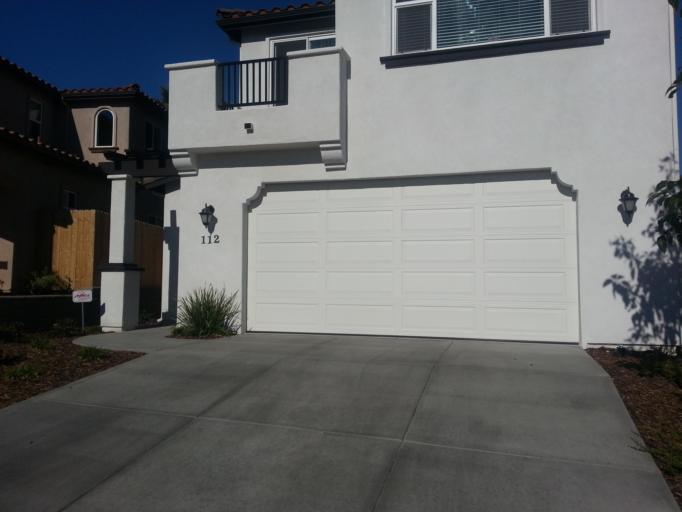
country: US
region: California
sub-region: San Luis Obispo County
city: Grover Beach
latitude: 35.1327
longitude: -120.6092
